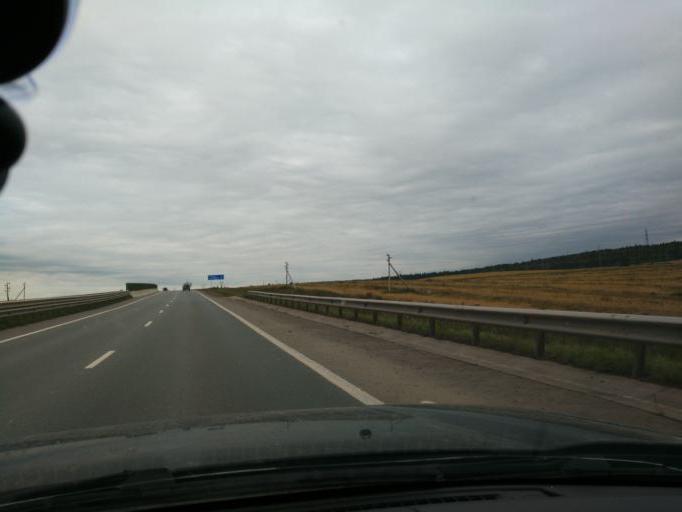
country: RU
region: Perm
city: Ferma
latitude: 57.9326
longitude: 56.3473
